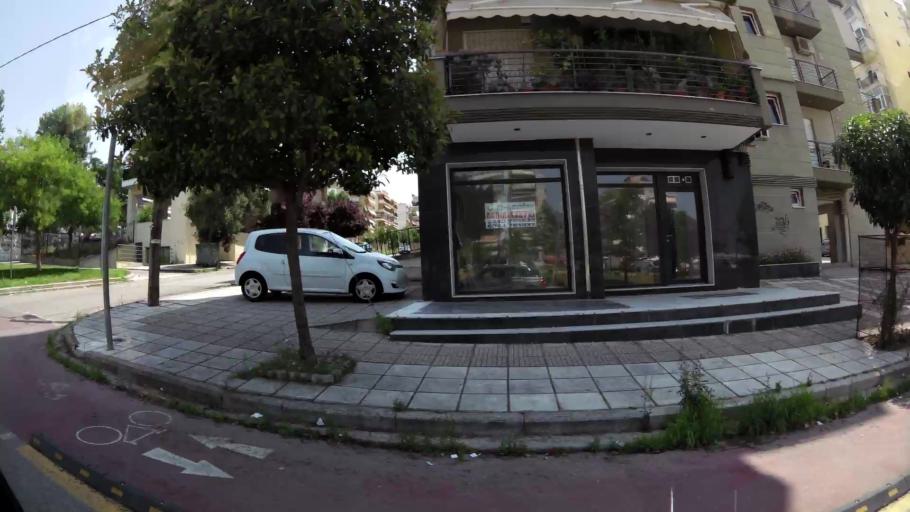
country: GR
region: Central Macedonia
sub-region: Nomos Thessalonikis
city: Evosmos
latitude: 40.6745
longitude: 22.9031
